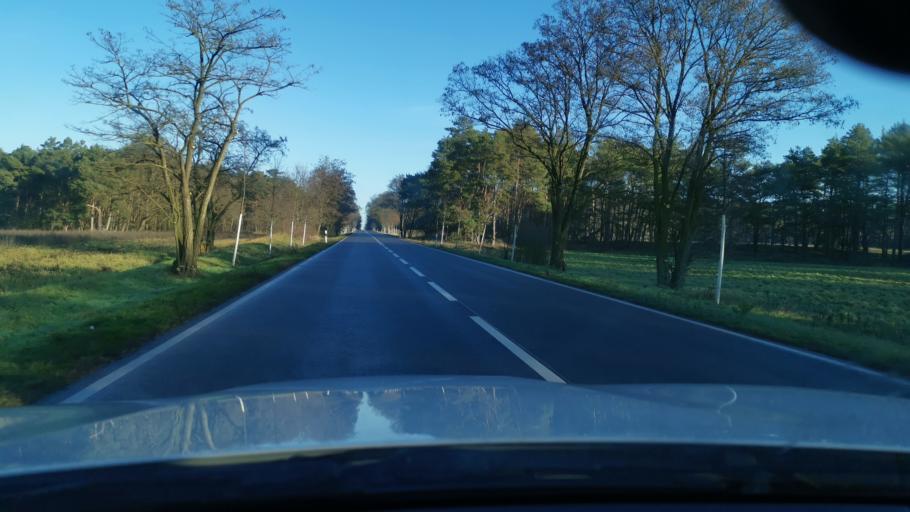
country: DE
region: Saxony-Anhalt
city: Abtsdorf
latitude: 51.9187
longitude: 12.6957
